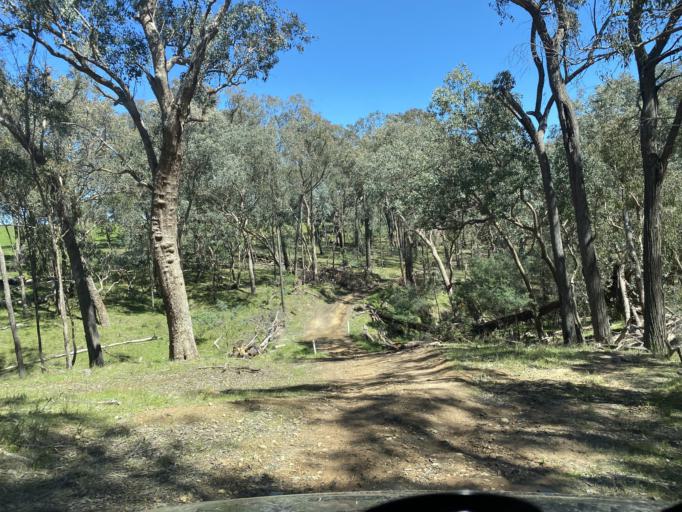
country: AU
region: Victoria
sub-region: Benalla
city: Benalla
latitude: -36.7050
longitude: 146.1564
